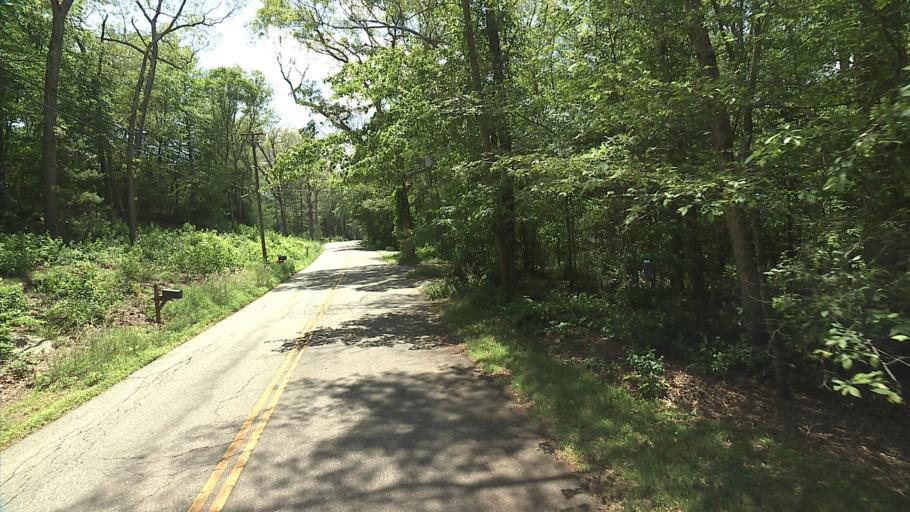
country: US
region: Connecticut
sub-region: New London County
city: Preston City
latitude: 41.5296
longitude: -71.8802
